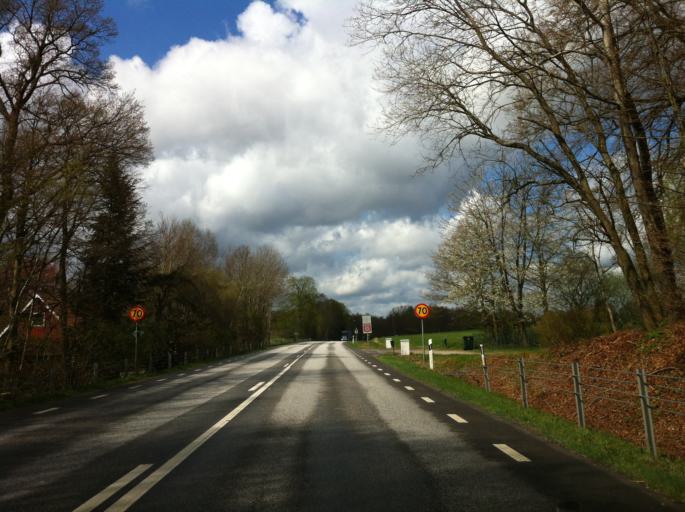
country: SE
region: Skane
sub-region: Hoors Kommun
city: Satofta
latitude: 55.9298
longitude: 13.5676
